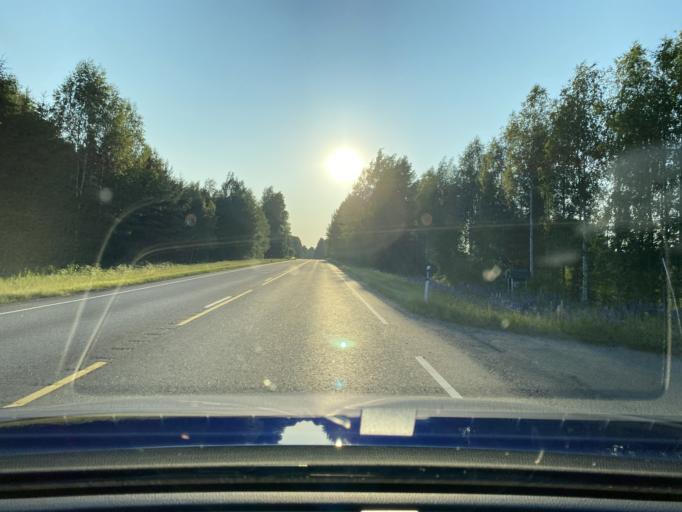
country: FI
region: Haeme
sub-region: Haemeenlinna
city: Renko
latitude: 60.7887
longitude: 24.1292
